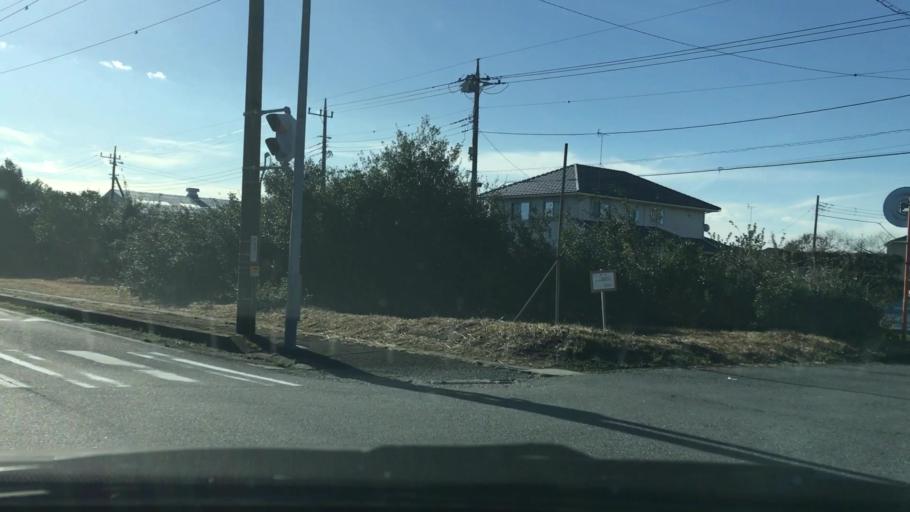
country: JP
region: Chiba
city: Omigawa
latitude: 35.8703
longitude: 140.7230
